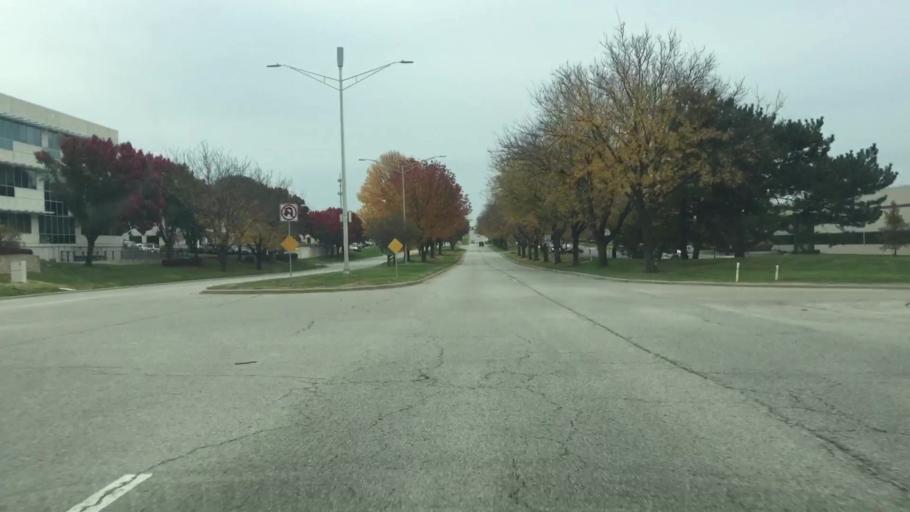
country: US
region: Kansas
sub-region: Johnson County
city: Lenexa
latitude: 38.9273
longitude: -94.7695
